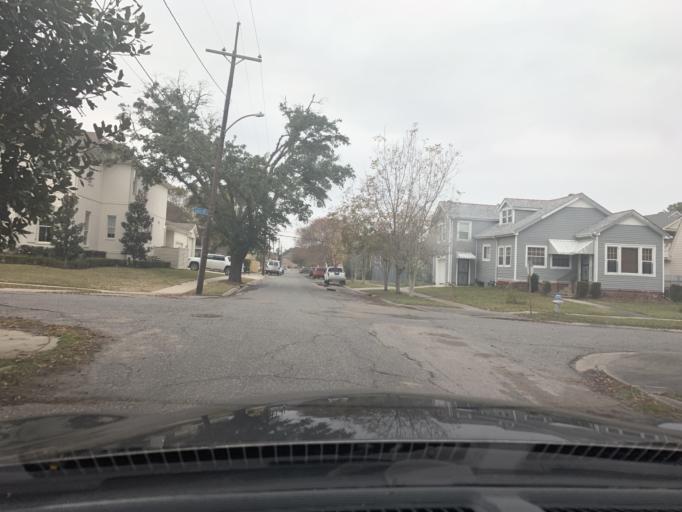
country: US
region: Louisiana
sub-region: Jefferson Parish
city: Metairie
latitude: 30.0105
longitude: -90.1085
